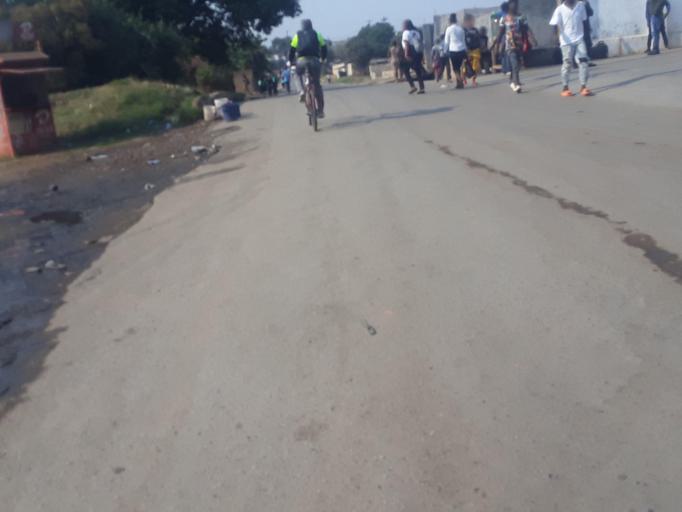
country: ZM
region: Lusaka
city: Lusaka
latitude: -15.3573
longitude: 28.3017
